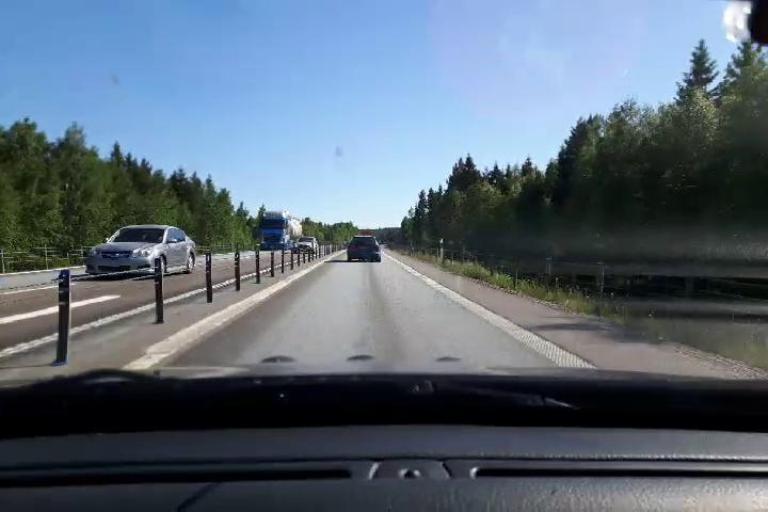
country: SE
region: Gaevleborg
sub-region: Gavle Kommun
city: Norrsundet
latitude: 60.9157
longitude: 17.0140
